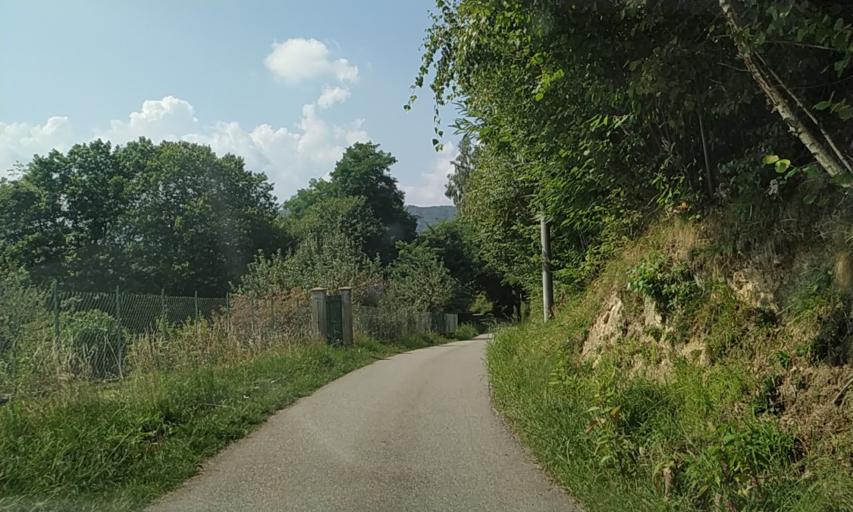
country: IT
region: Piedmont
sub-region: Provincia di Vercelli
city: Cellio
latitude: 45.7471
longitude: 8.3154
